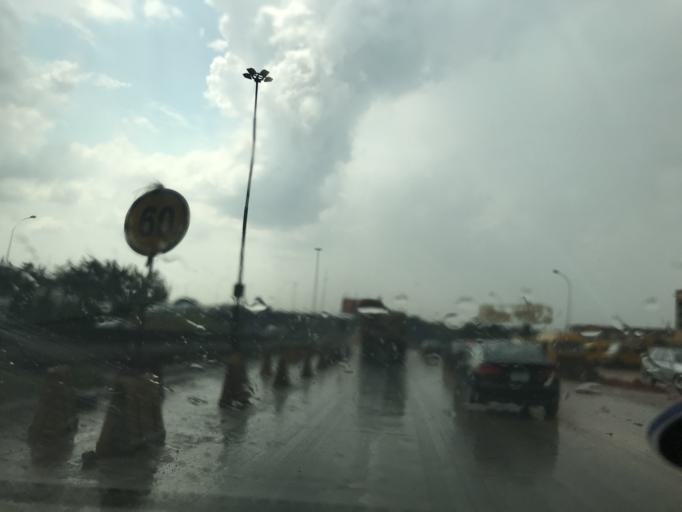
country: NG
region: Lagos
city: Oshodi
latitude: 6.5506
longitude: 3.3397
